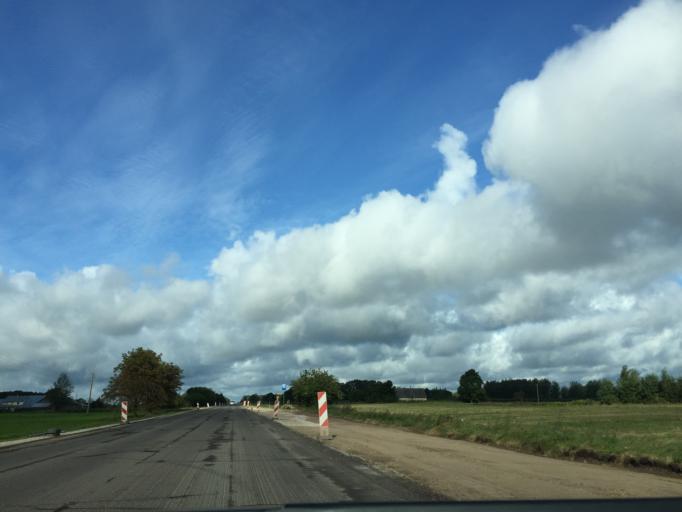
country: LV
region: Tukuma Rajons
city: Tukums
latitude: 56.9257
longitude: 23.2338
